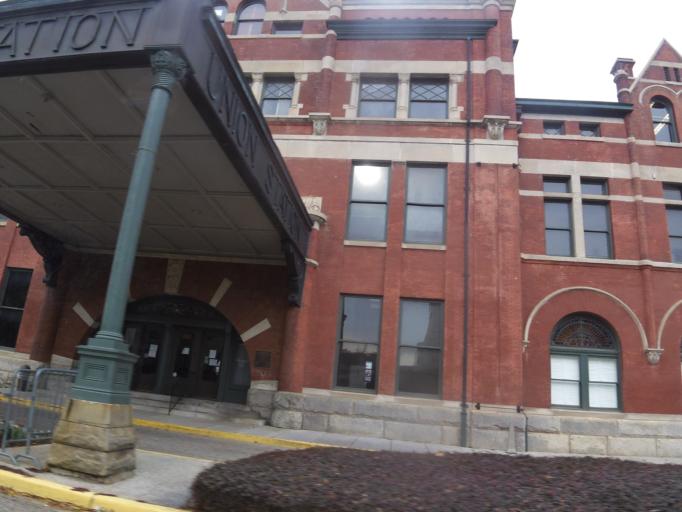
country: US
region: Alabama
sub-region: Montgomery County
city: Montgomery
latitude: 32.3805
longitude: -86.3138
